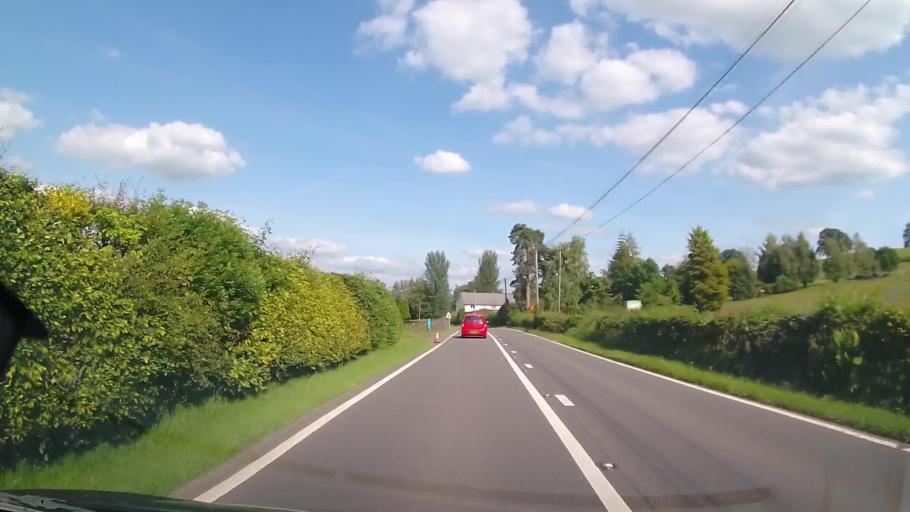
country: GB
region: Wales
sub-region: Sir Powys
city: Llanfyllin
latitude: 52.6698
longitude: -3.3973
